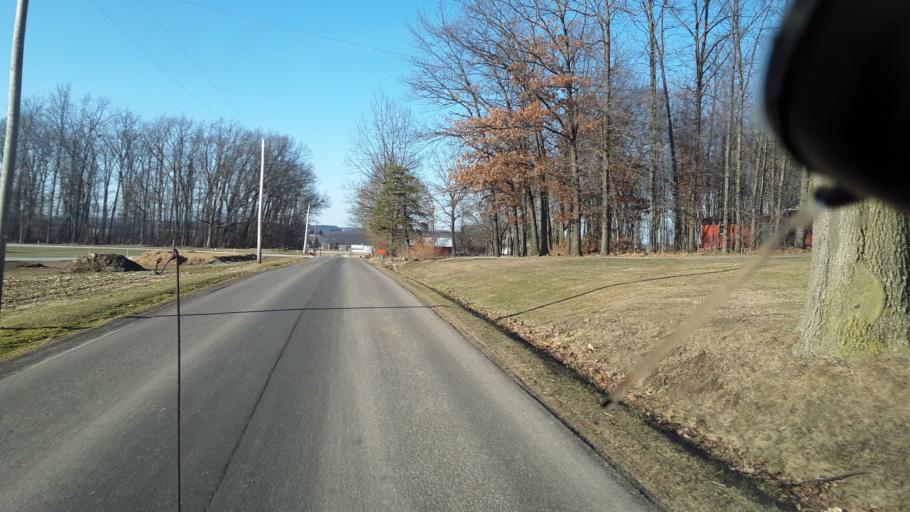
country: US
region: Ohio
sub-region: Wayne County
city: Apple Creek
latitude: 40.7175
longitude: -81.8427
